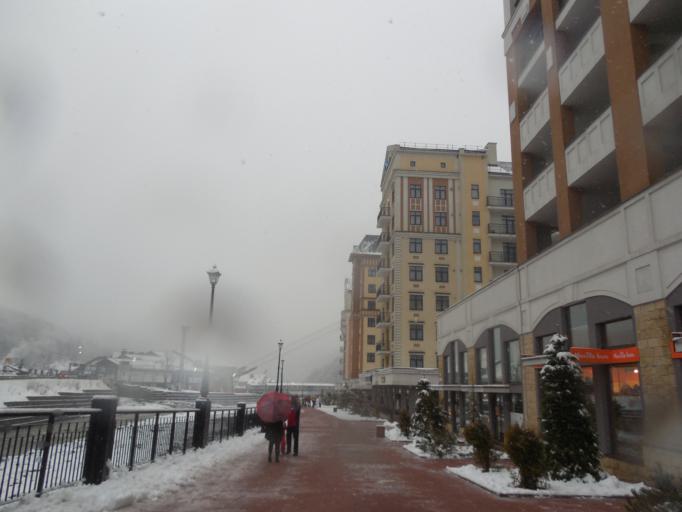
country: RU
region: Krasnodarskiy
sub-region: Sochi City
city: Krasnaya Polyana
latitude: 43.6751
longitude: 40.2879
